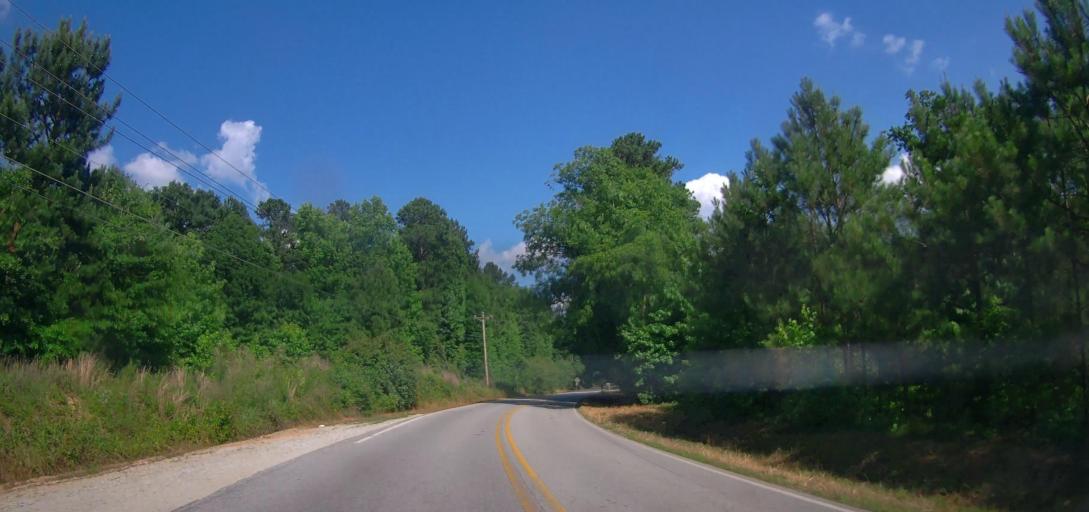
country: US
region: Georgia
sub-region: Spalding County
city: East Griffin
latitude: 33.2913
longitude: -84.2079
